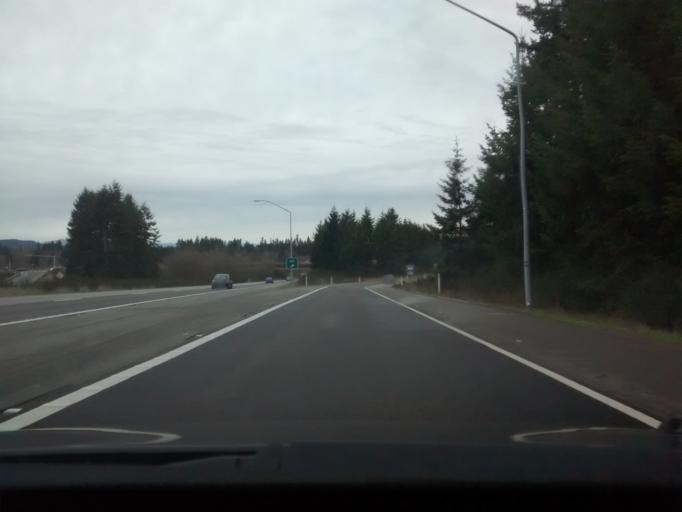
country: US
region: Washington
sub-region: Kitsap County
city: Bethel
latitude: 47.4988
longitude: -122.6431
